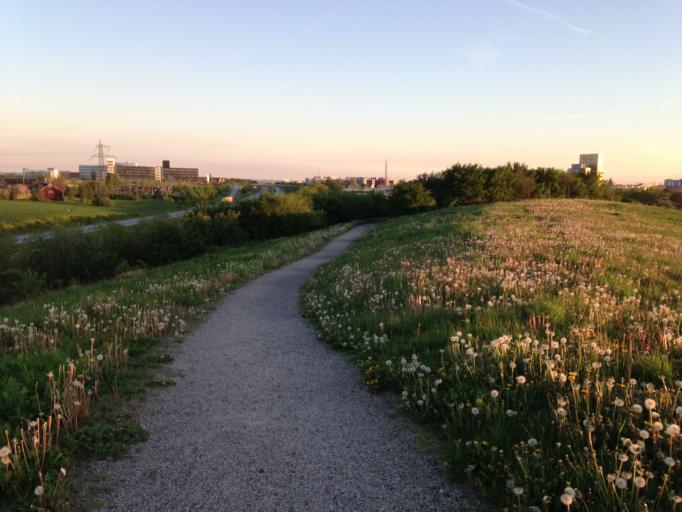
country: SE
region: Skane
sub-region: Lunds Kommun
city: Lund
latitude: 55.7263
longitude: 13.2264
